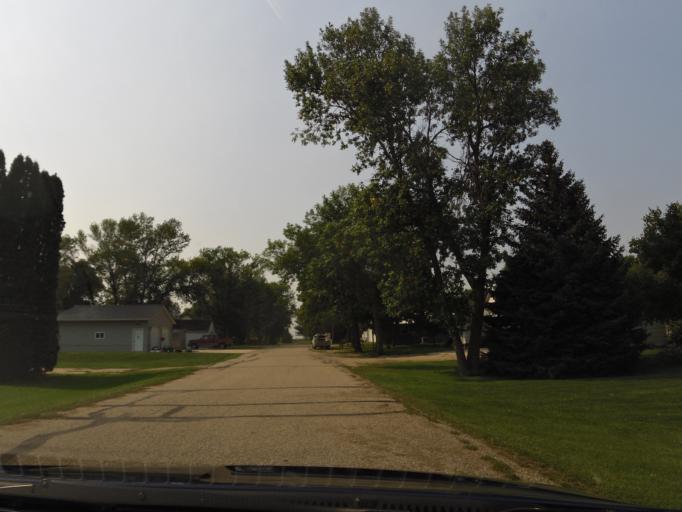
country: US
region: South Dakota
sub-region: Roberts County
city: Sisseton
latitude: 45.8568
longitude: -97.1046
